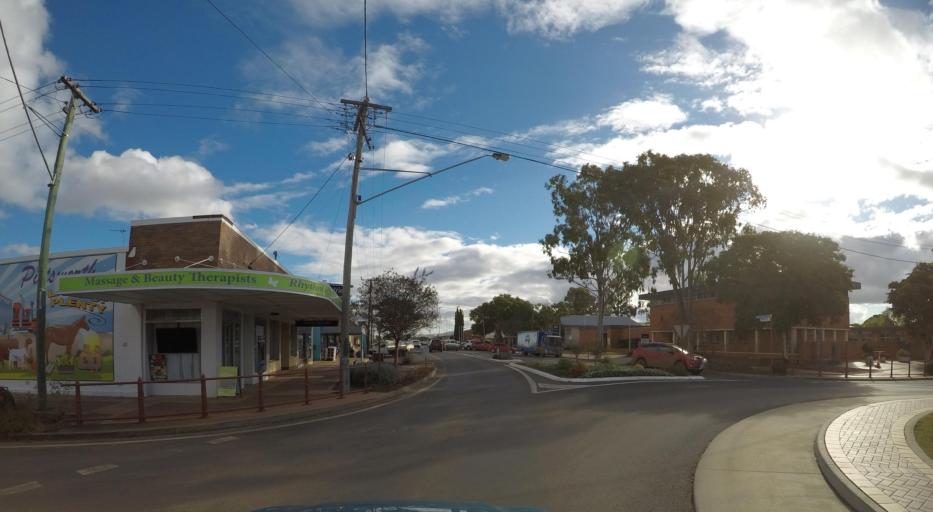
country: AU
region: Queensland
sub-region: Toowoomba
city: Westbrook
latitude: -27.7159
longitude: 151.6346
